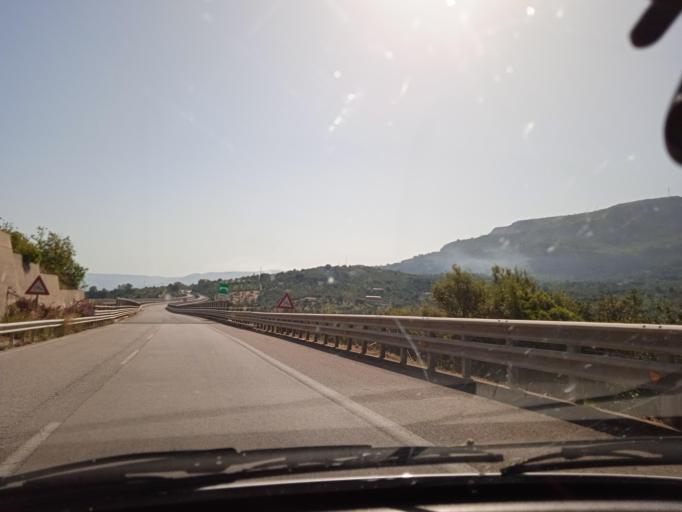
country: IT
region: Sicily
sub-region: Messina
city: Acquedolci
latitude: 38.0455
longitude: 14.5547
